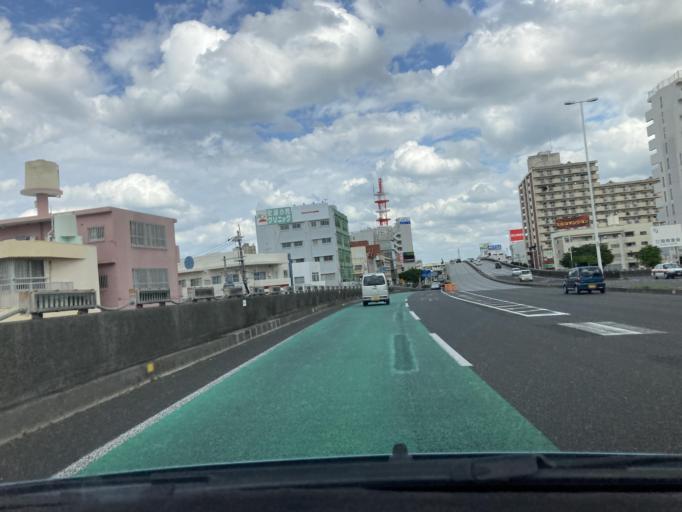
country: JP
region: Okinawa
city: Naha-shi
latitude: 26.2386
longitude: 127.6879
